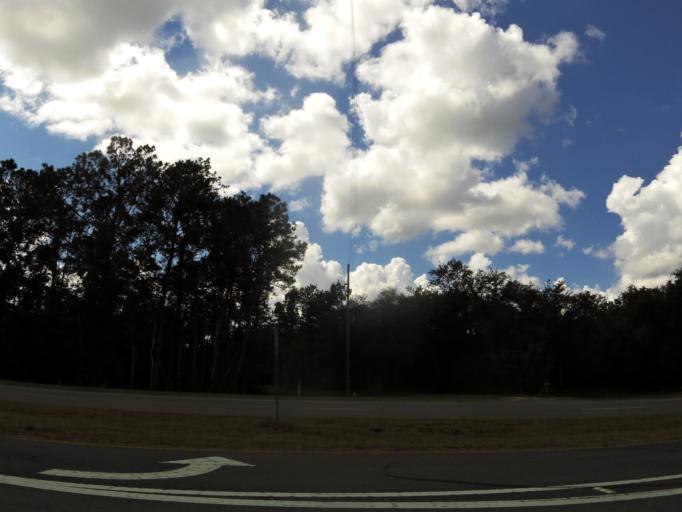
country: US
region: Georgia
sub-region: Charlton County
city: Folkston
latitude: 30.8079
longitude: -81.9961
